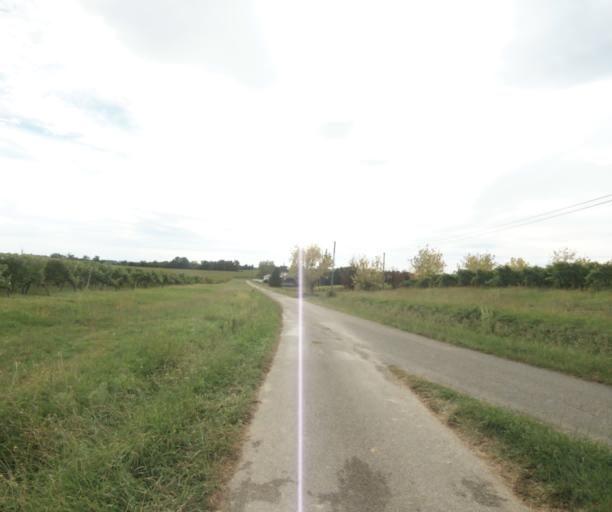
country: FR
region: Midi-Pyrenees
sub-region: Departement du Gers
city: Cazaubon
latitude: 43.8840
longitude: -0.1342
